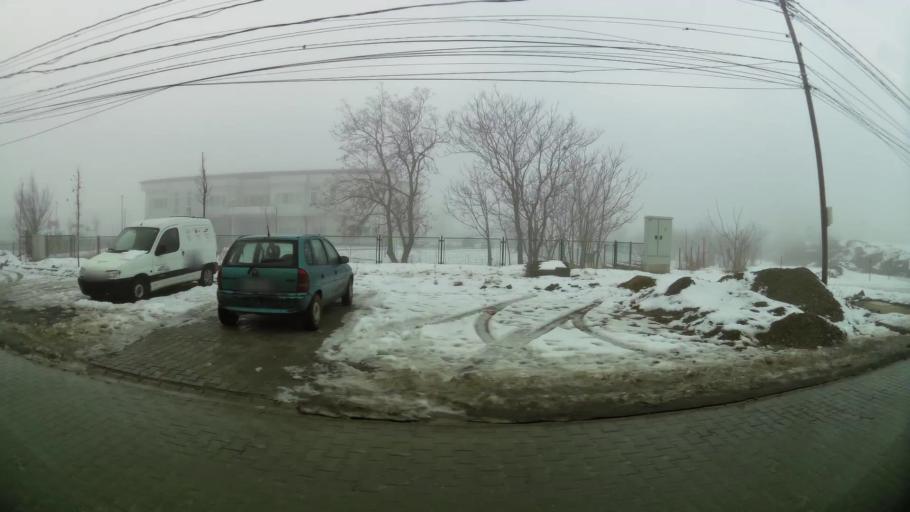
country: XK
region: Pristina
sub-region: Komuna e Prishtines
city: Pristina
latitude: 42.6424
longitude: 21.1438
